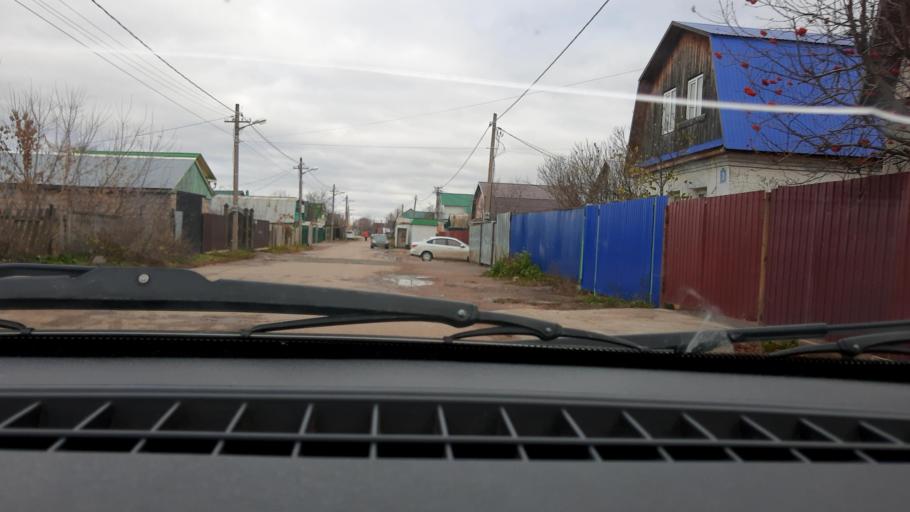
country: RU
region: Bashkortostan
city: Ufa
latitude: 54.7355
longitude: 55.9059
